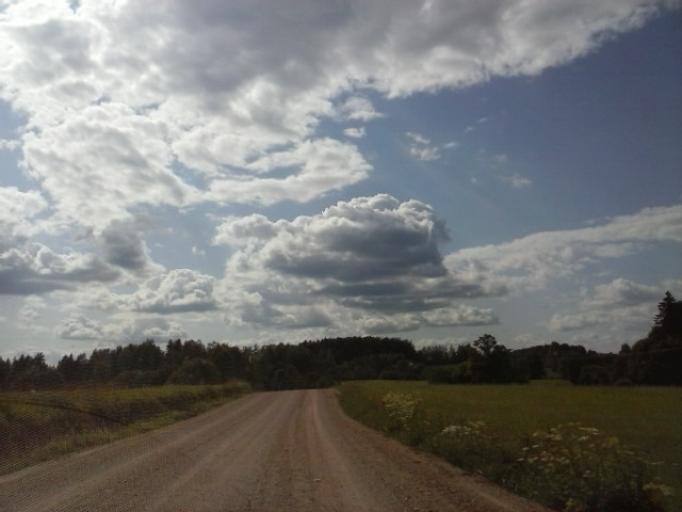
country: EE
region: Vorumaa
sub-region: Voru linn
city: Voru
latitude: 57.7490
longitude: 27.1416
